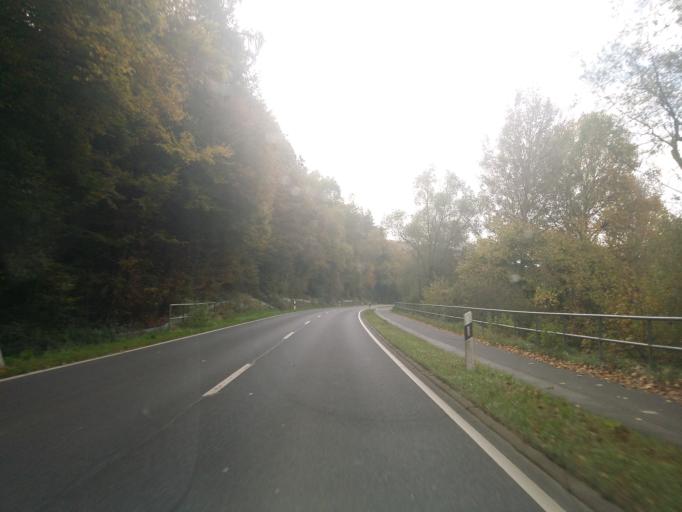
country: DE
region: Hesse
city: Eppstein
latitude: 50.1636
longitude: 8.3772
